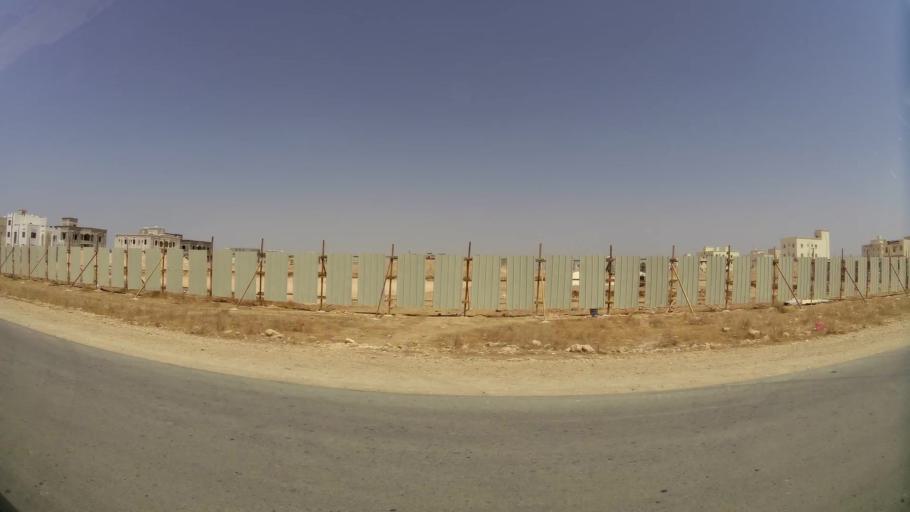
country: OM
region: Zufar
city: Salalah
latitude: 17.0747
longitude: 54.1997
